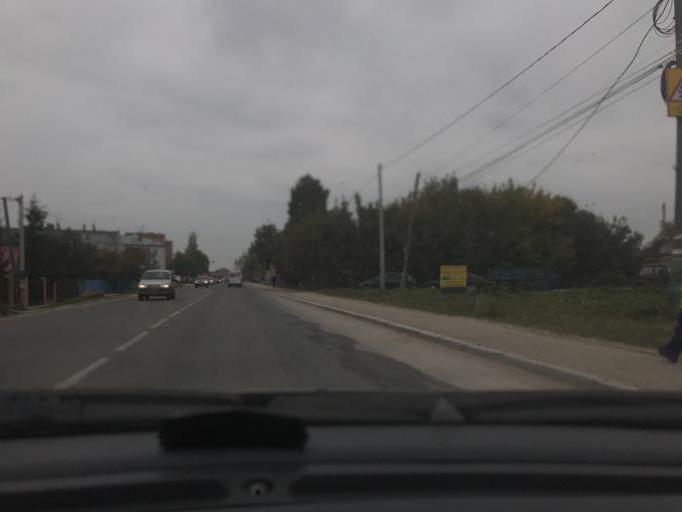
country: RU
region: Kaluga
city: Kaluga
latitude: 54.5153
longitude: 36.3354
